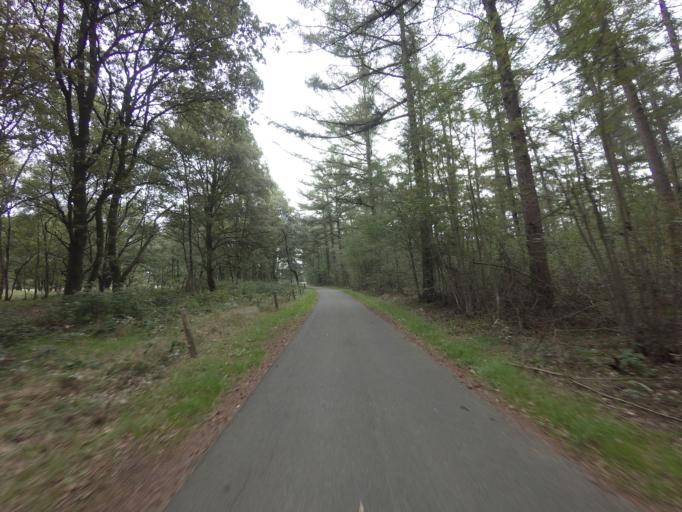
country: NL
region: Drenthe
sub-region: Gemeente Assen
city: Assen
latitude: 52.9118
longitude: 6.5040
